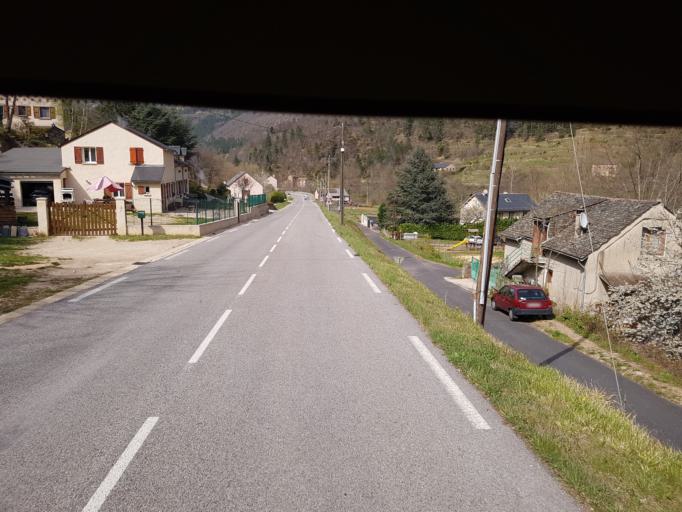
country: FR
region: Languedoc-Roussillon
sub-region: Departement de la Lozere
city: Florac
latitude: 44.3080
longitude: 3.5976
